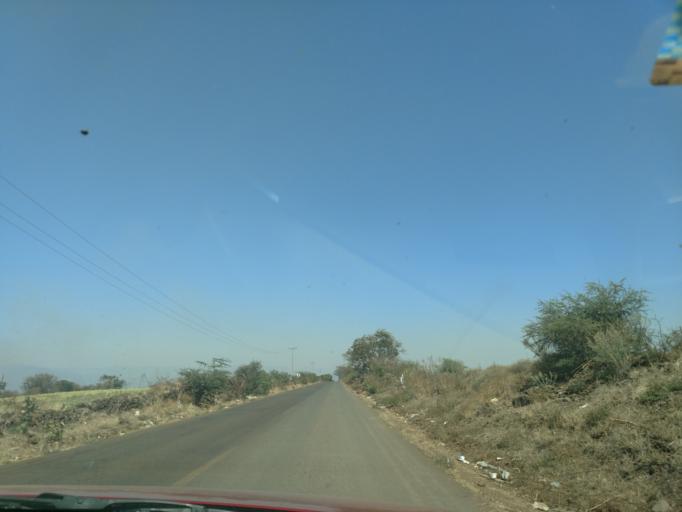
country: MX
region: Nayarit
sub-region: Tepic
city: La Corregidora
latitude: 21.4976
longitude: -104.7014
